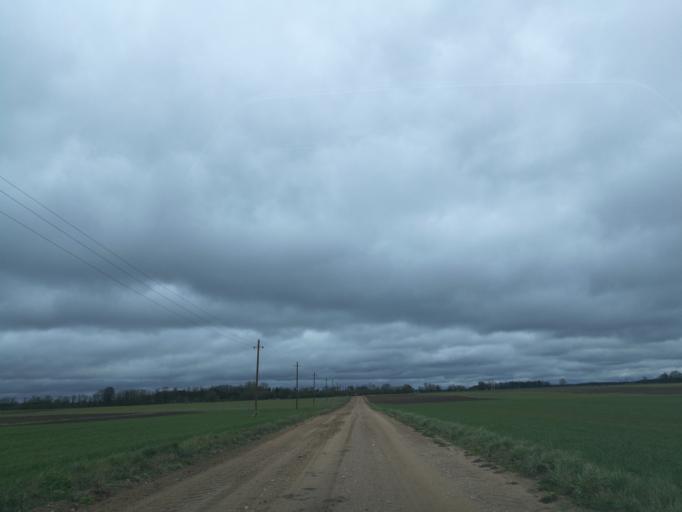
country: LT
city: Ariogala
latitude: 55.3800
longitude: 23.3339
